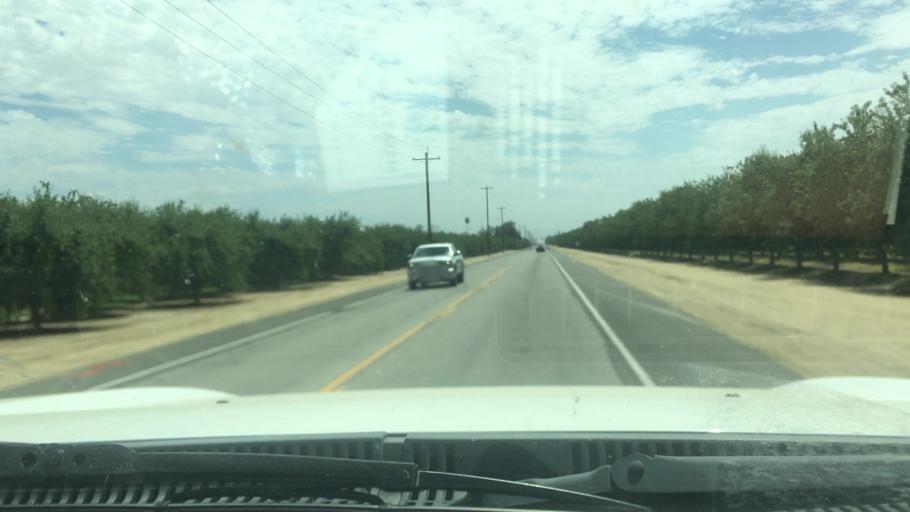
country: US
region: California
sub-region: Kern County
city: Wasco
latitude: 35.5579
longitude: -119.3405
